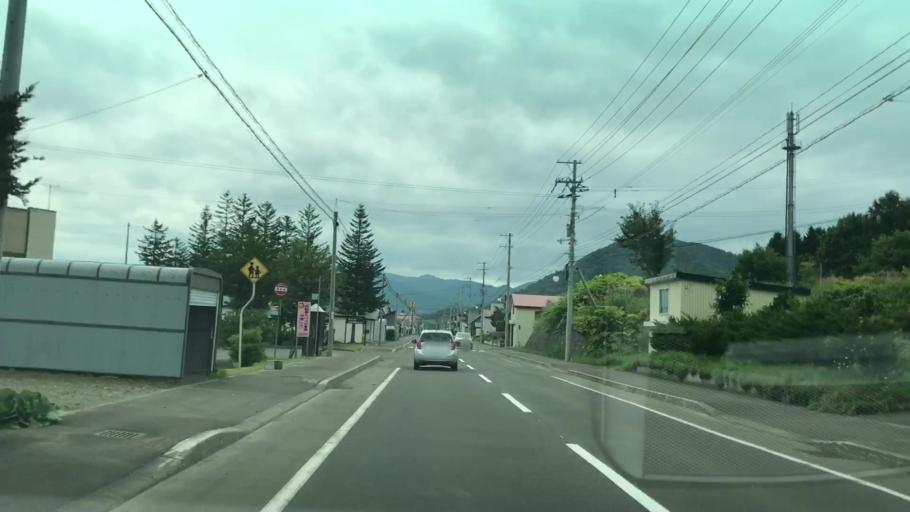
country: JP
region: Hokkaido
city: Yoichi
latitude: 43.0874
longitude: 140.8155
